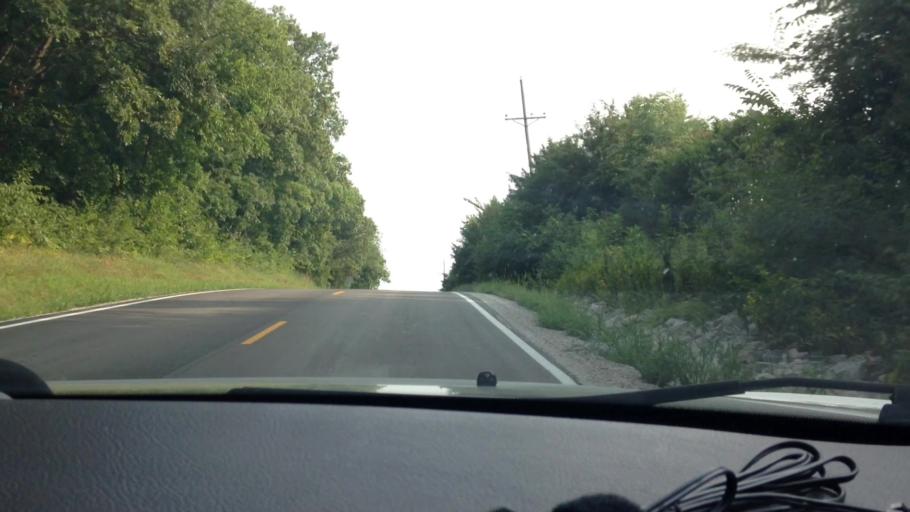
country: US
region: Missouri
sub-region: Platte County
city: Platte City
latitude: 39.4034
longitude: -94.7797
